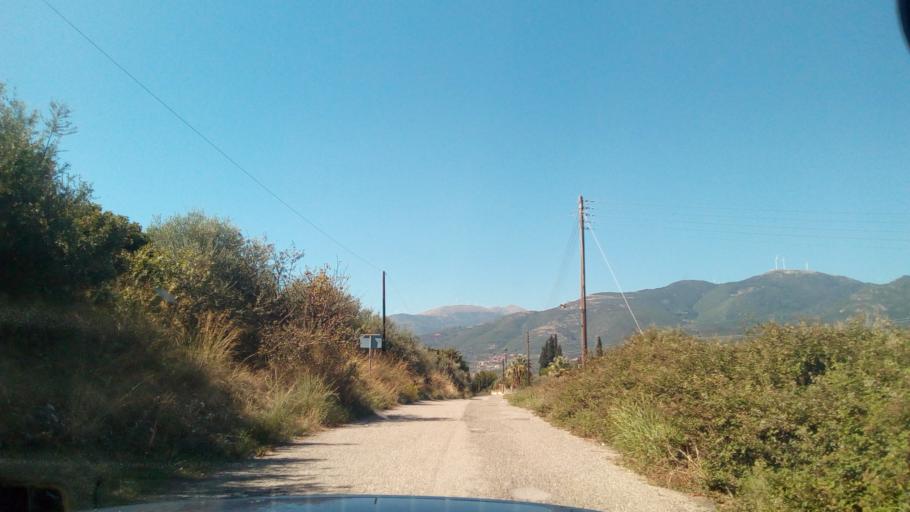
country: GR
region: West Greece
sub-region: Nomos Aitolias kai Akarnanias
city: Nafpaktos
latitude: 38.4093
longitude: 21.8996
